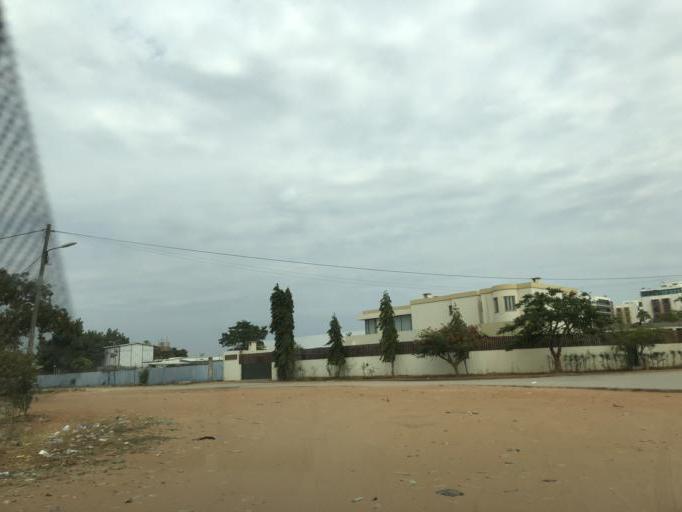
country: AO
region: Luanda
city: Luanda
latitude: -8.8906
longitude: 13.1919
